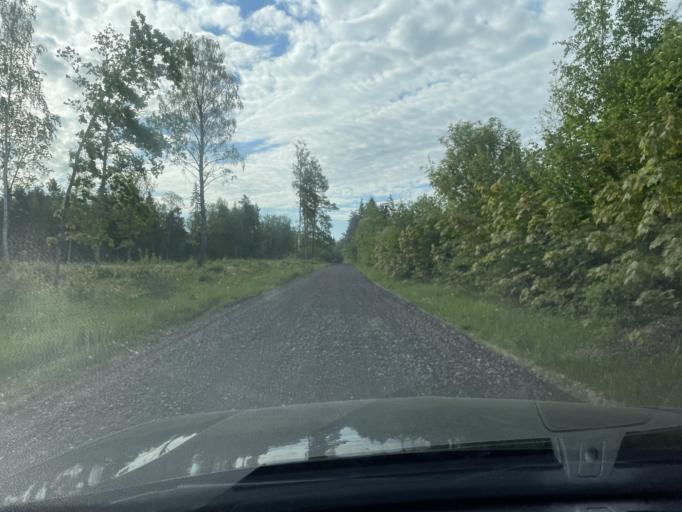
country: EE
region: Harju
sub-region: Keila linn
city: Keila
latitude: 59.3062
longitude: 24.2960
